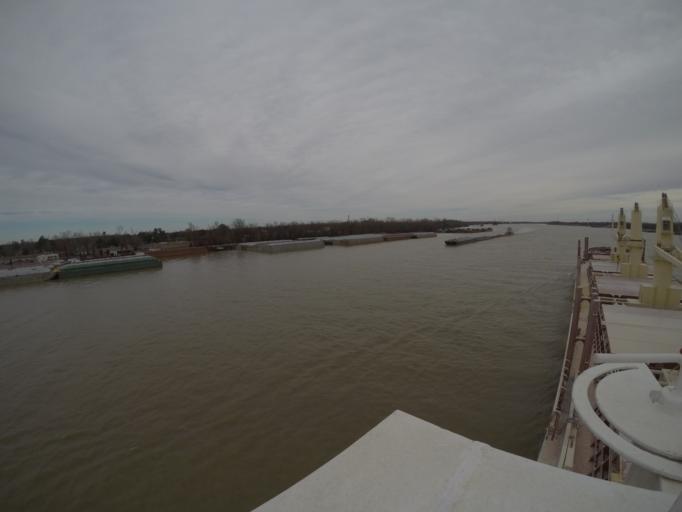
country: US
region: Louisiana
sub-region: Saint John the Baptist Parish
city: Reserve
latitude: 30.0467
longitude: -90.5361
